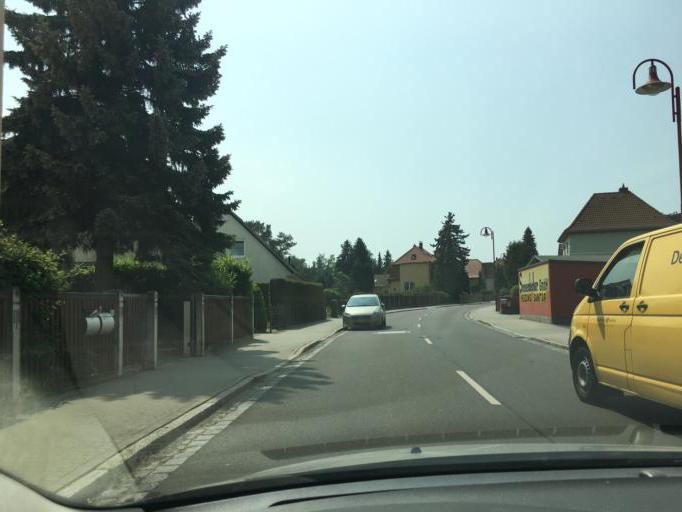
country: DE
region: Saxony
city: Grossposna
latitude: 51.2711
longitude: 12.4958
